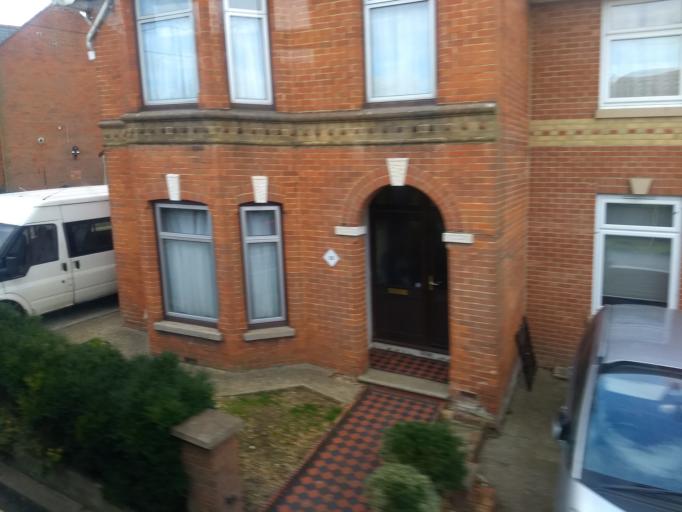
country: GB
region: England
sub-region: Isle of Wight
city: Newport
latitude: 50.6927
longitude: -1.3158
